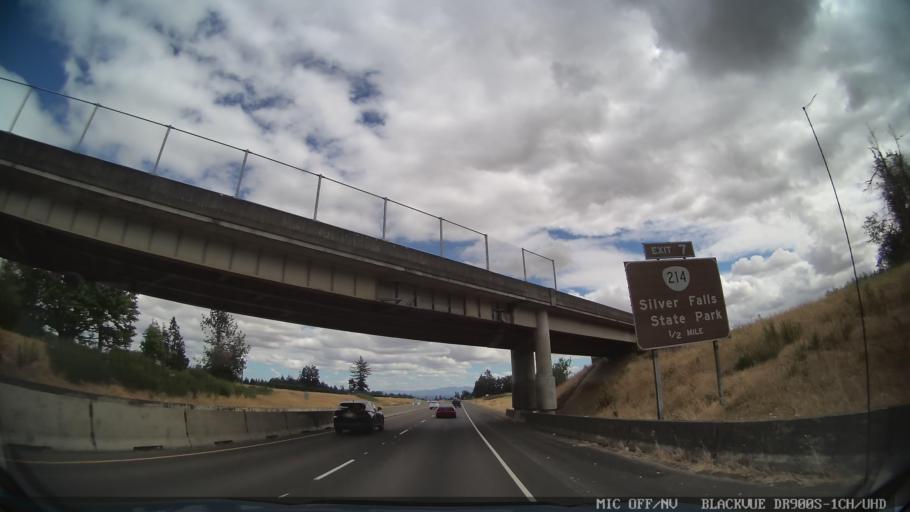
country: US
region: Oregon
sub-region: Marion County
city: Turner
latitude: 44.8803
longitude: -122.9135
